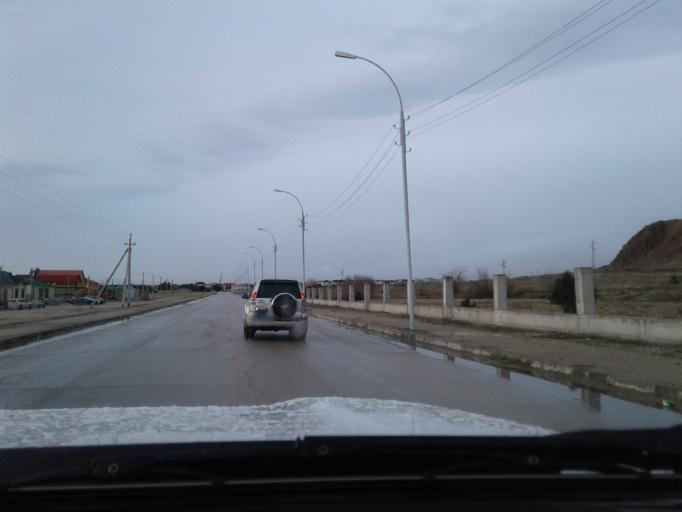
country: TM
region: Balkan
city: Balkanabat
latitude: 39.5281
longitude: 54.3607
